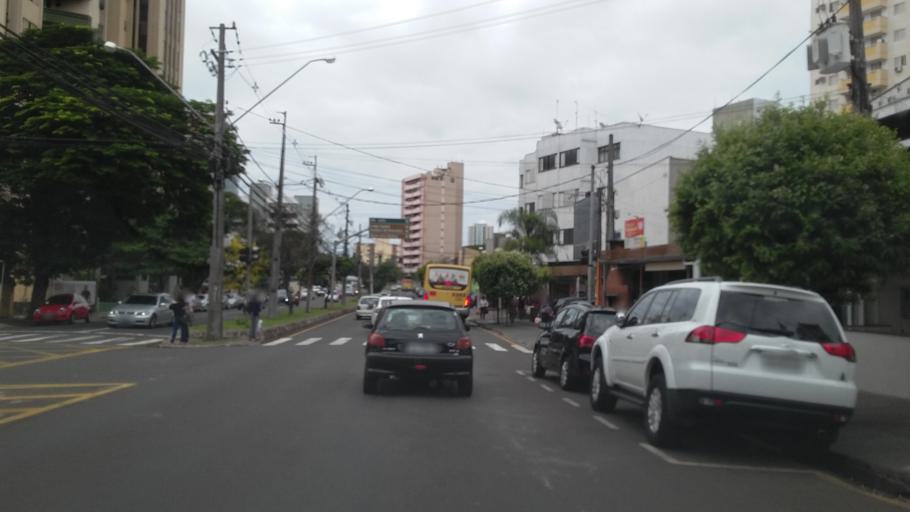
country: BR
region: Parana
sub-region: Londrina
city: Londrina
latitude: -23.3209
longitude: -51.1668
